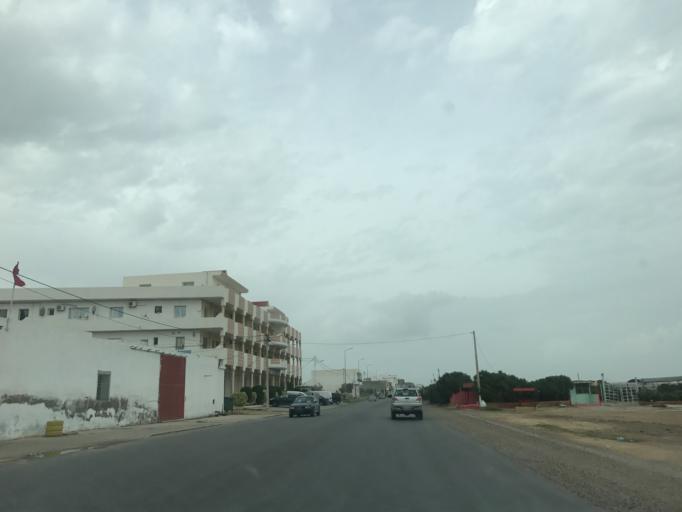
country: TN
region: Al Munastir
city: Qusaybat al Madyuni
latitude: 35.7030
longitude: 10.8265
